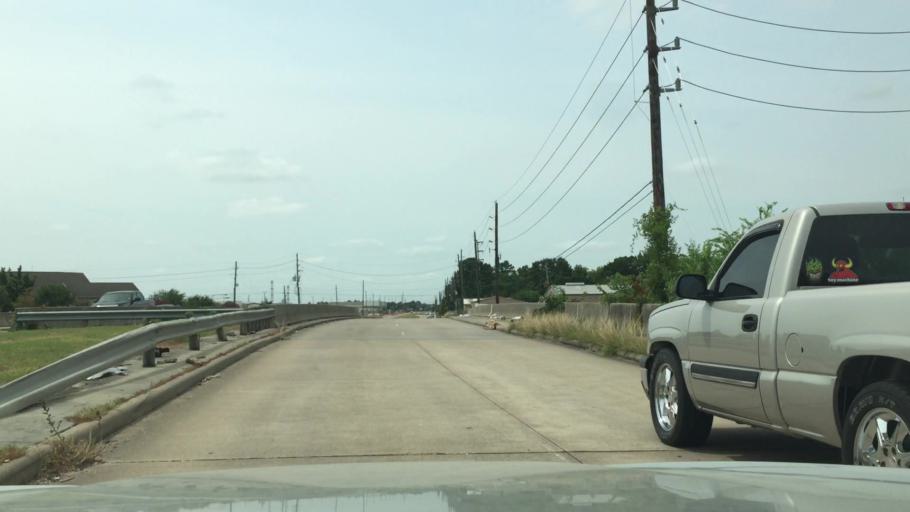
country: US
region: Texas
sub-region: Harris County
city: Jersey Village
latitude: 29.9495
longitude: -95.5470
